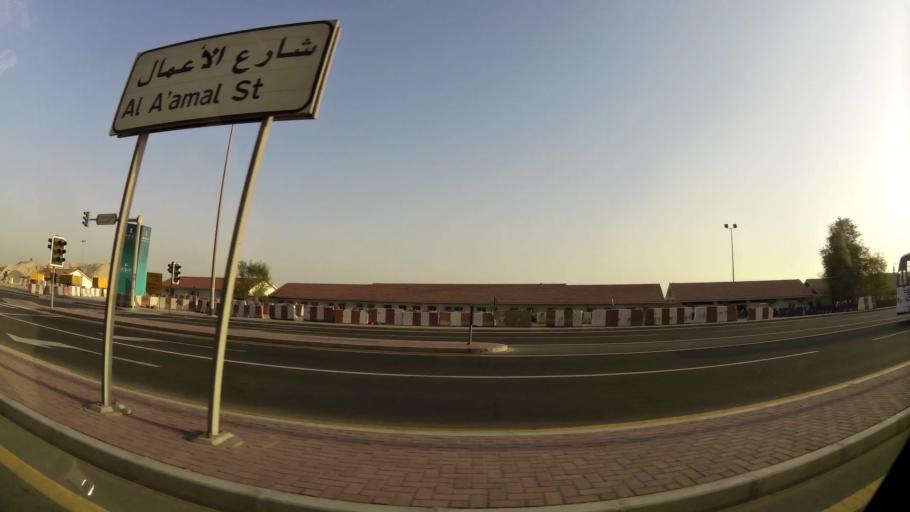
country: AE
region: Dubai
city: Dubai
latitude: 25.1796
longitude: 55.2633
